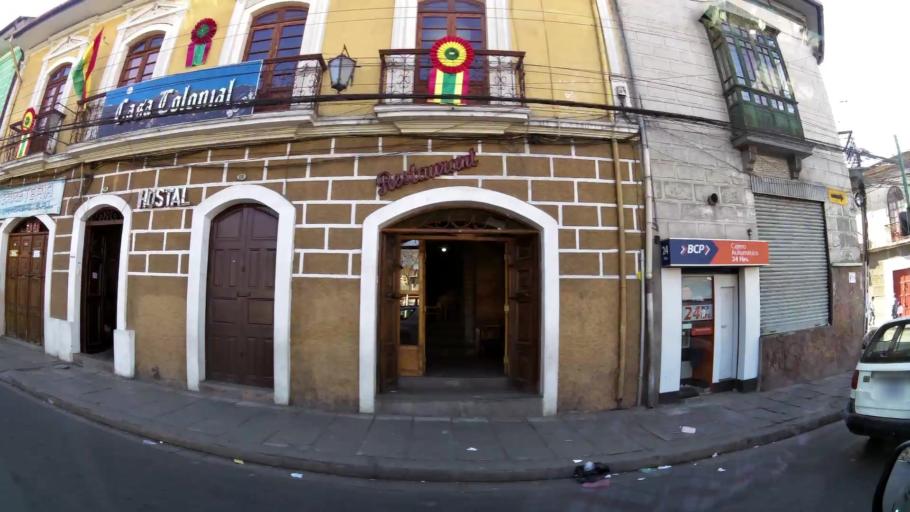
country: BO
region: La Paz
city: La Paz
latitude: -16.5019
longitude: -68.1353
